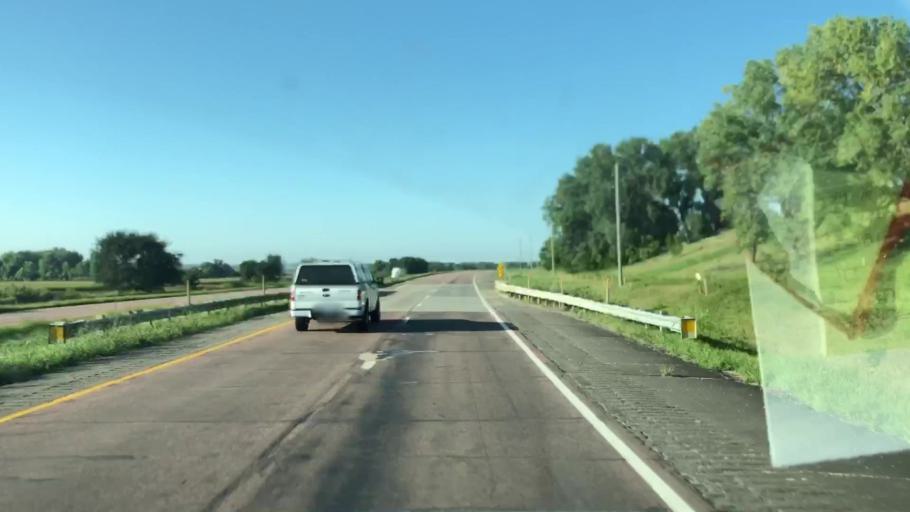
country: US
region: Iowa
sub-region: Woodbury County
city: Sioux City
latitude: 42.5860
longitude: -96.3092
